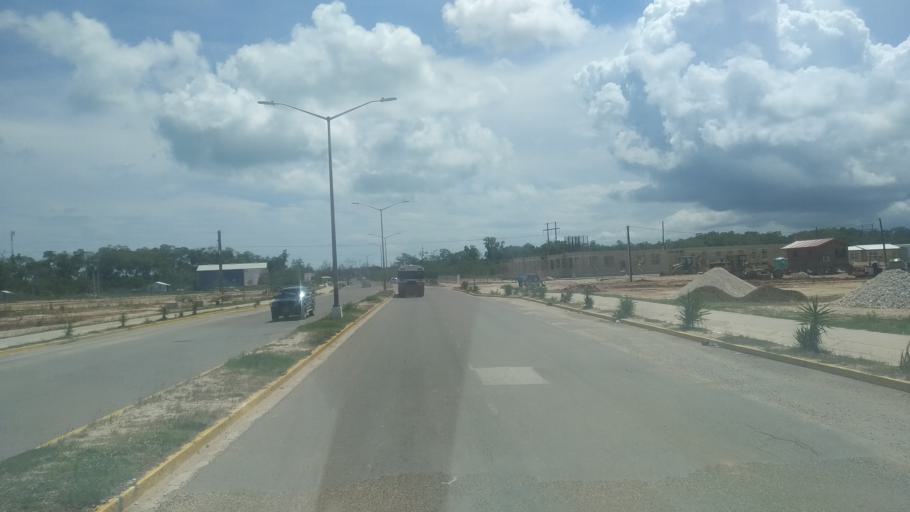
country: BZ
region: Belize
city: Belize City
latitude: 17.5052
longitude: -88.2219
